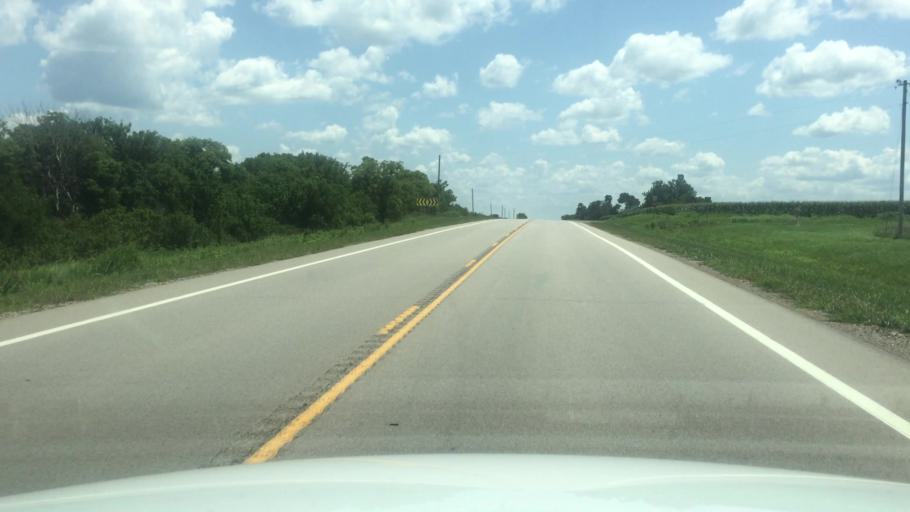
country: US
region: Kansas
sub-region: Brown County
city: Horton
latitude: 39.6101
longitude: -95.3444
